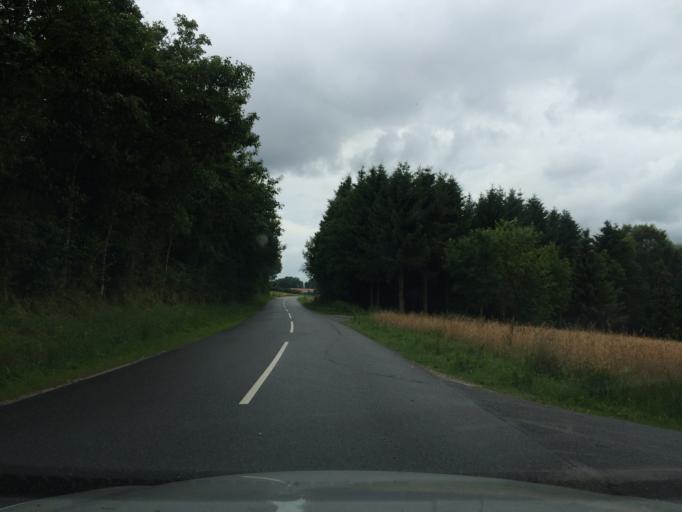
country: DK
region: Central Jutland
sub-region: Silkeborg Kommune
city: Svejbaek
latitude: 56.2249
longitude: 9.7038
